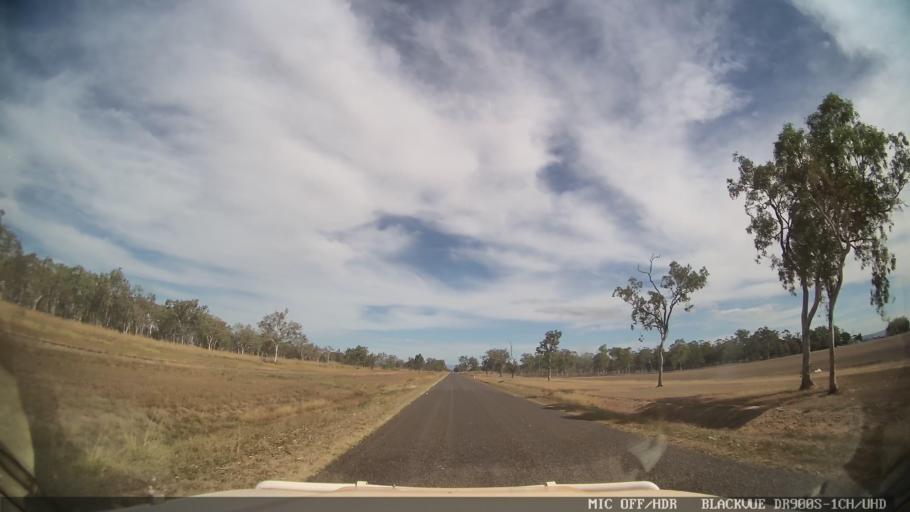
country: AU
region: Queensland
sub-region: Tablelands
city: Mareeba
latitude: -16.9333
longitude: 145.4177
